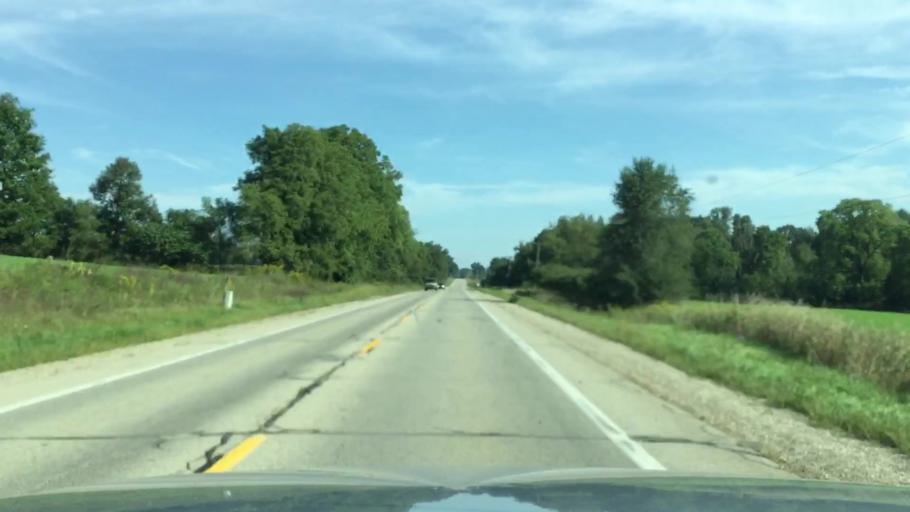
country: US
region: Michigan
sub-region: Lenawee County
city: Manitou Beach-Devils Lake
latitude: 41.9473
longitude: -84.3671
